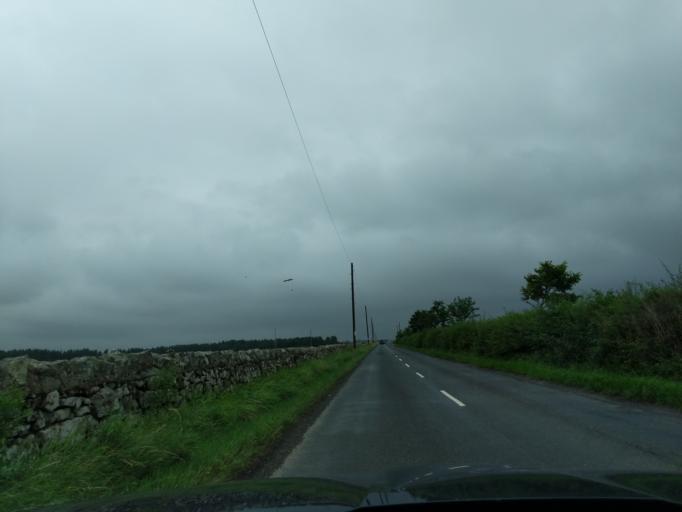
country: GB
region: England
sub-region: Northumberland
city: Ford
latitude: 55.6588
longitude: -2.1081
